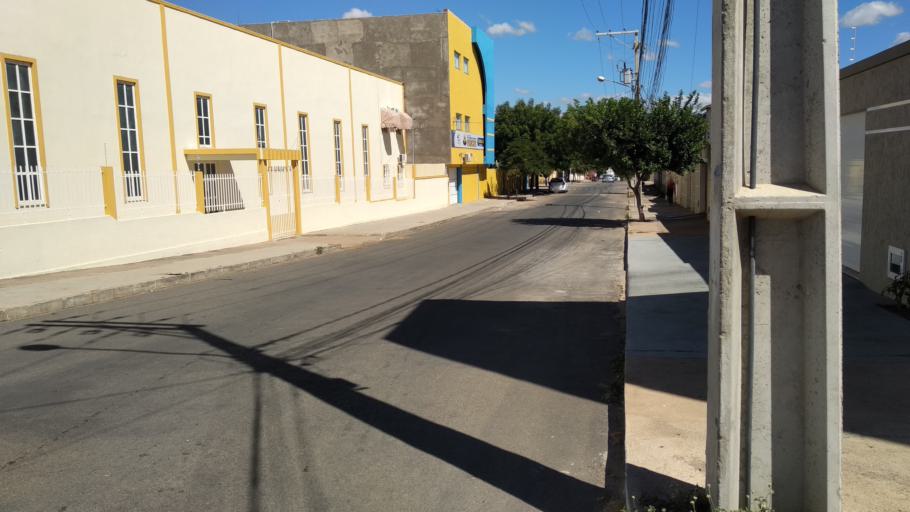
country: BR
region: Bahia
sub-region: Guanambi
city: Guanambi
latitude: -14.2294
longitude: -42.7761
